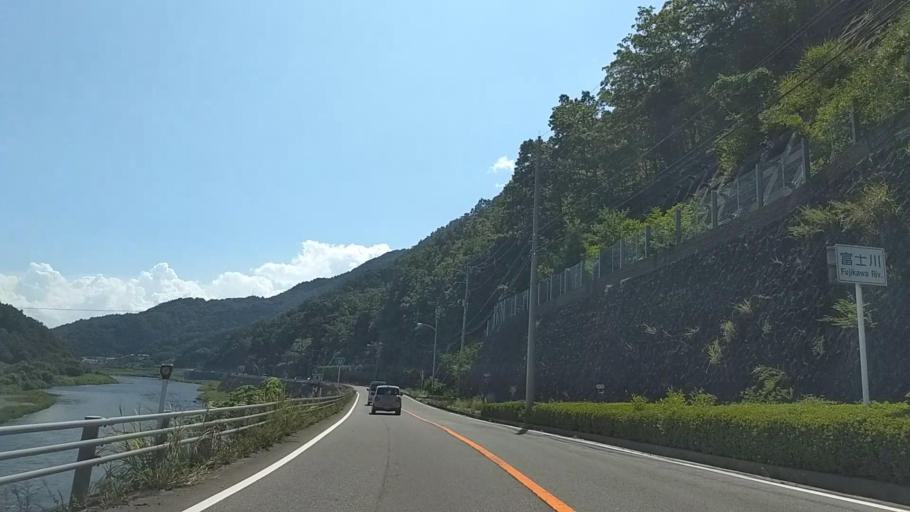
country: JP
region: Yamanashi
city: Ryuo
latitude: 35.5357
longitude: 138.4516
